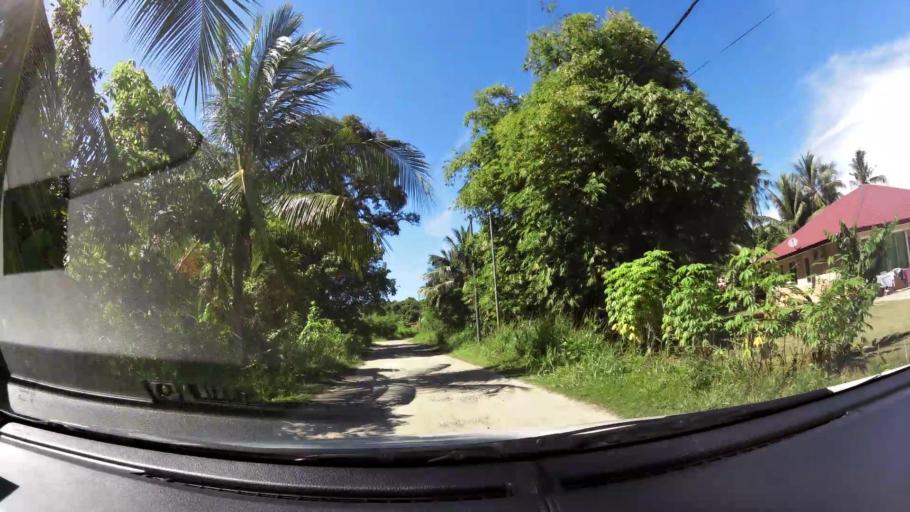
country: BN
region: Brunei and Muara
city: Bandar Seri Begawan
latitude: 5.0076
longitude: 115.0579
